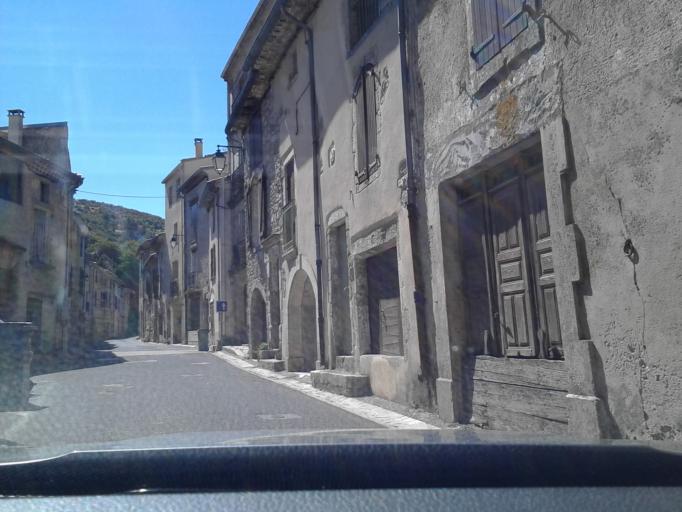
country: FR
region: Languedoc-Roussillon
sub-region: Departement de l'Herault
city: Montpeyroux
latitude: 43.7890
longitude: 3.4602
